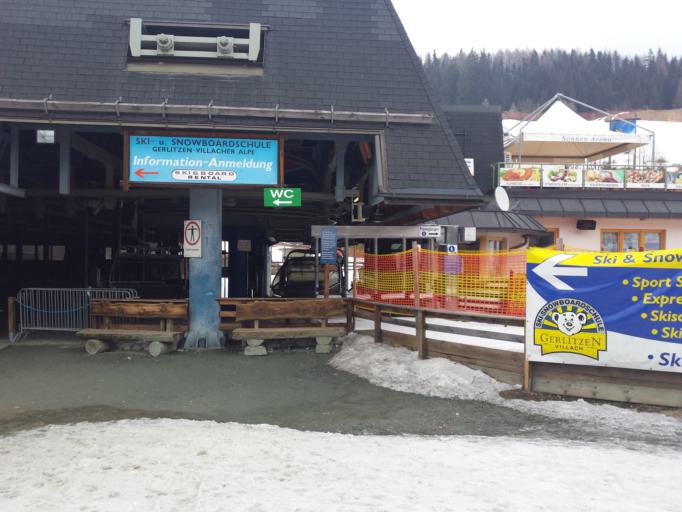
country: AT
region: Carinthia
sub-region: Politischer Bezirk Villach Land
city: Arriach
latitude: 46.6815
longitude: 13.8996
